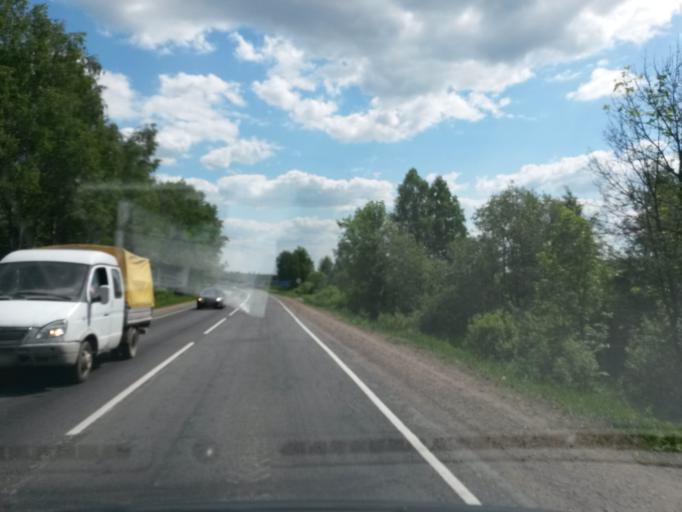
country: RU
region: Jaroslavl
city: Yaroslavl
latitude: 57.5524
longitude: 39.8831
